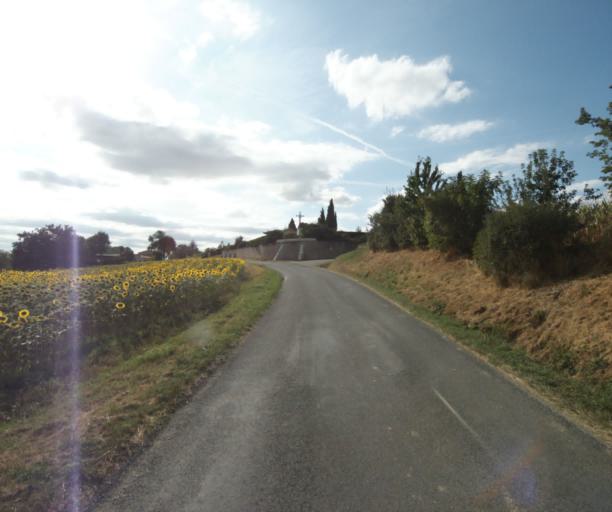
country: FR
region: Midi-Pyrenees
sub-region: Departement du Tarn
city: Puylaurens
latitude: 43.5203
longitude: 1.9886
